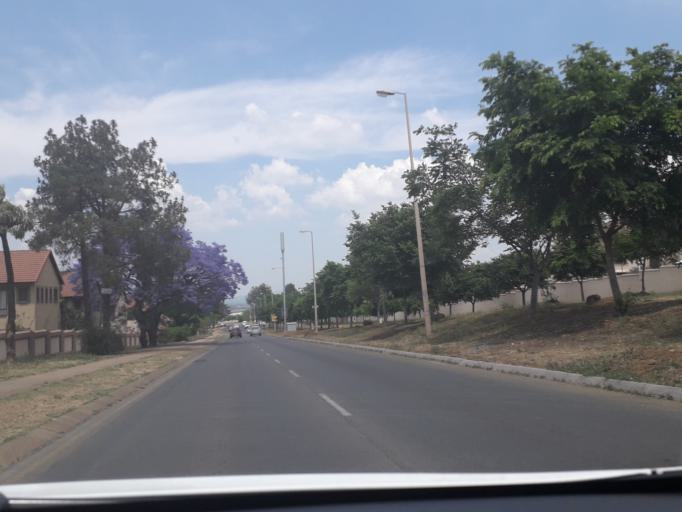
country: ZA
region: Gauteng
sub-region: City of Johannesburg Metropolitan Municipality
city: Midrand
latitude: -25.9931
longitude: 28.1065
